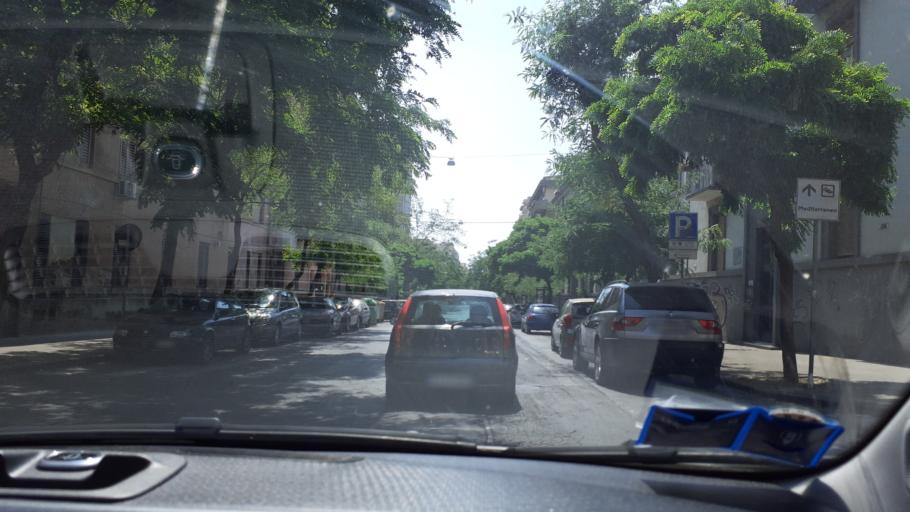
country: IT
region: Sicily
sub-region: Catania
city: Catania
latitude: 37.5129
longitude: 15.0744
